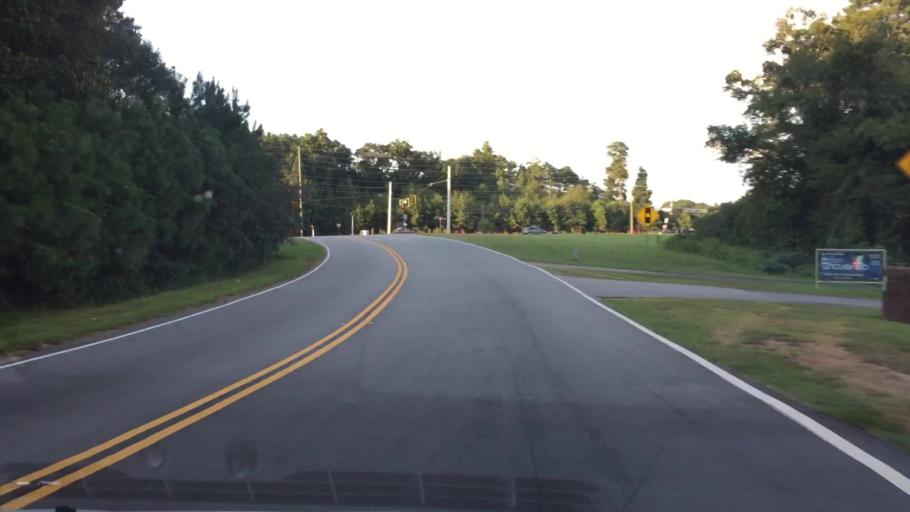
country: US
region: Georgia
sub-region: Henry County
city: McDonough
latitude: 33.4583
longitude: -84.1961
